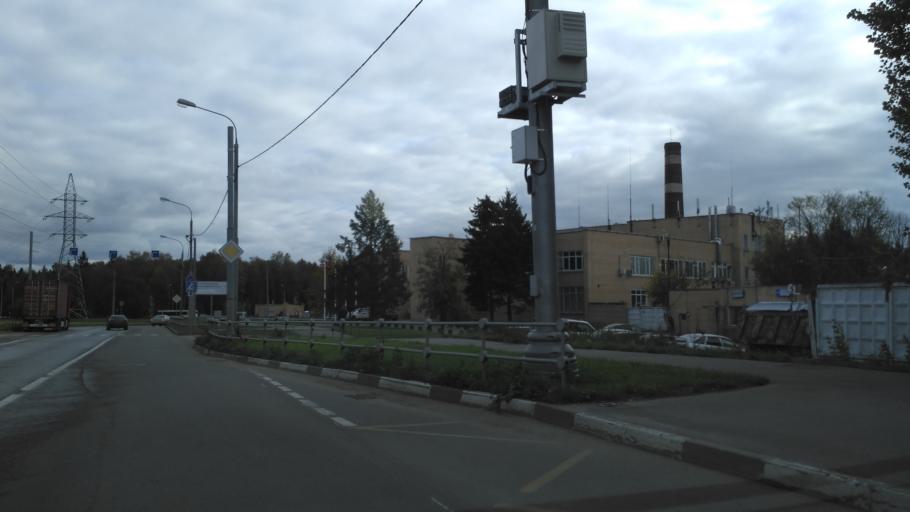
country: RU
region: Moskovskaya
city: Alabushevo
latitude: 56.0087
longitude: 37.1651
